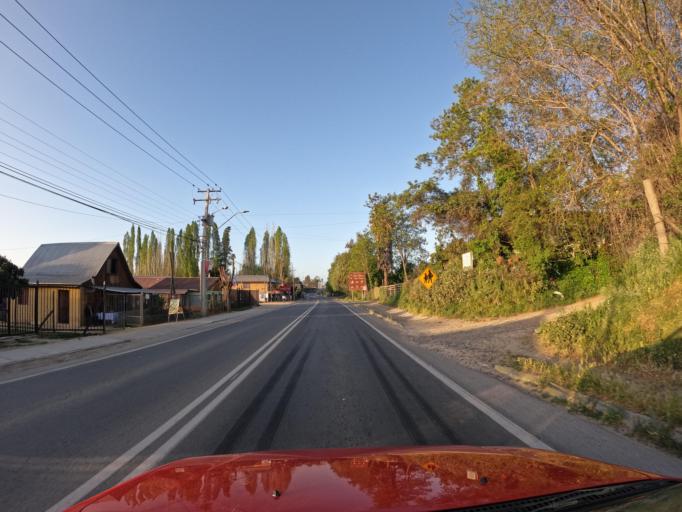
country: CL
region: O'Higgins
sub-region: Provincia de Cachapoal
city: San Vicente
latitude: -34.1817
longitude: -71.4007
